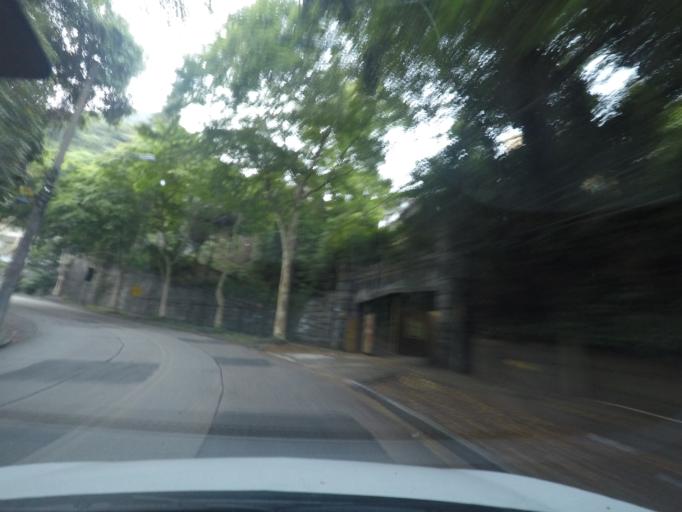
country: BR
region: Rio de Janeiro
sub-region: Rio De Janeiro
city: Rio de Janeiro
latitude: -22.9491
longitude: -43.2610
